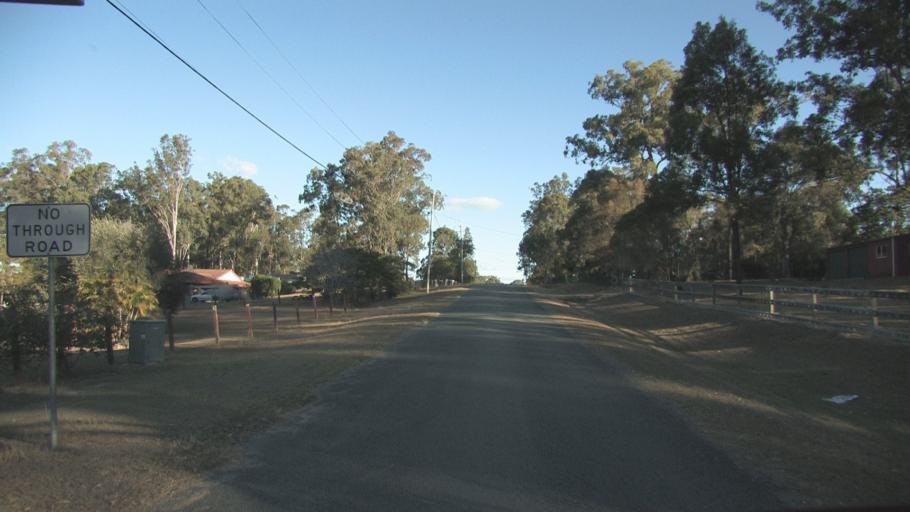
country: AU
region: Queensland
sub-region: Logan
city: Cedar Vale
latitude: -27.8634
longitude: 152.9746
